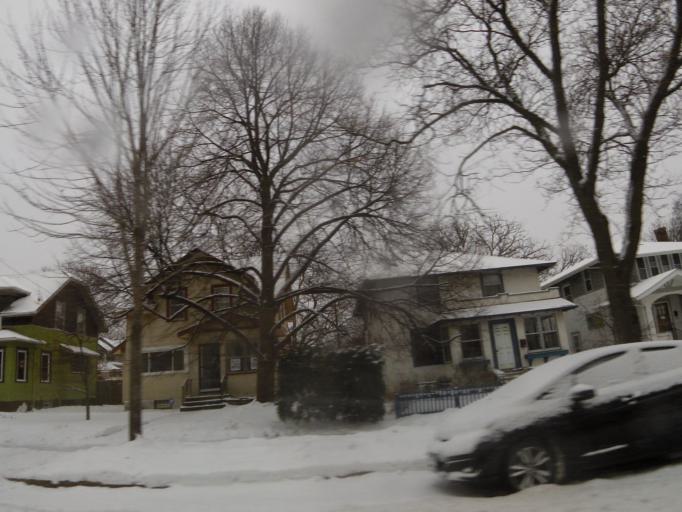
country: US
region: Minnesota
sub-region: Hennepin County
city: Minneapolis
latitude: 44.9334
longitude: -93.2650
